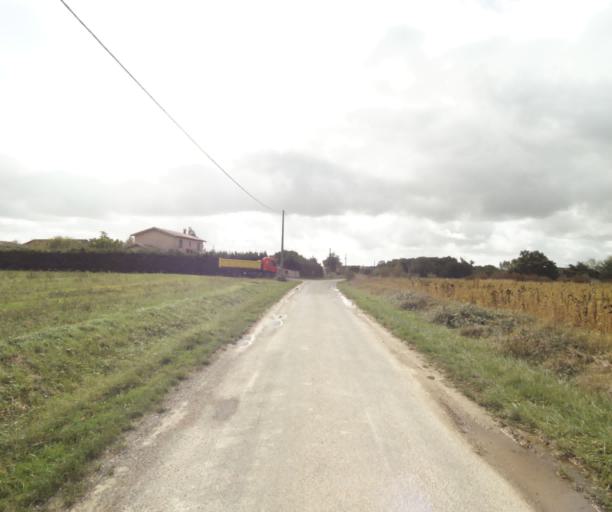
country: FR
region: Midi-Pyrenees
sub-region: Departement du Tarn-et-Garonne
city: Beaumont-de-Lomagne
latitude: 43.8692
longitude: 1.0686
